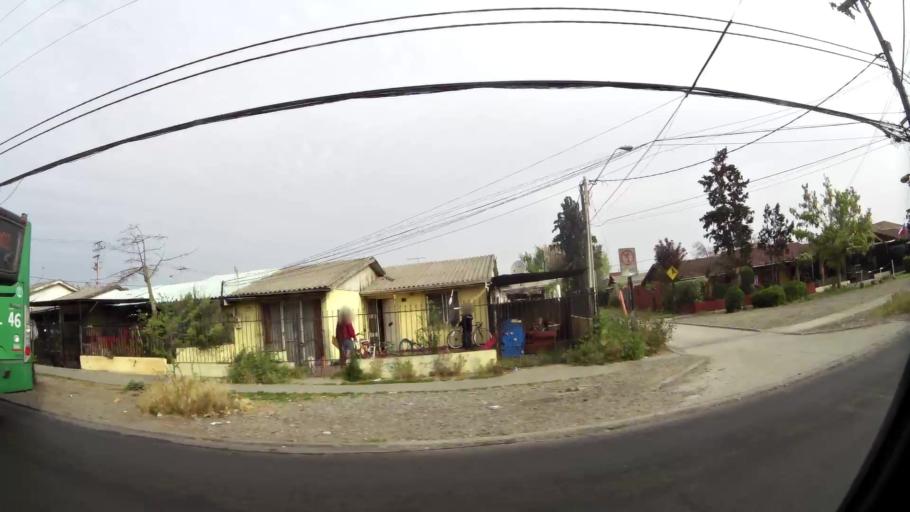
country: CL
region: Santiago Metropolitan
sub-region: Provincia de Santiago
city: Lo Prado
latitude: -33.5176
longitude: -70.7640
